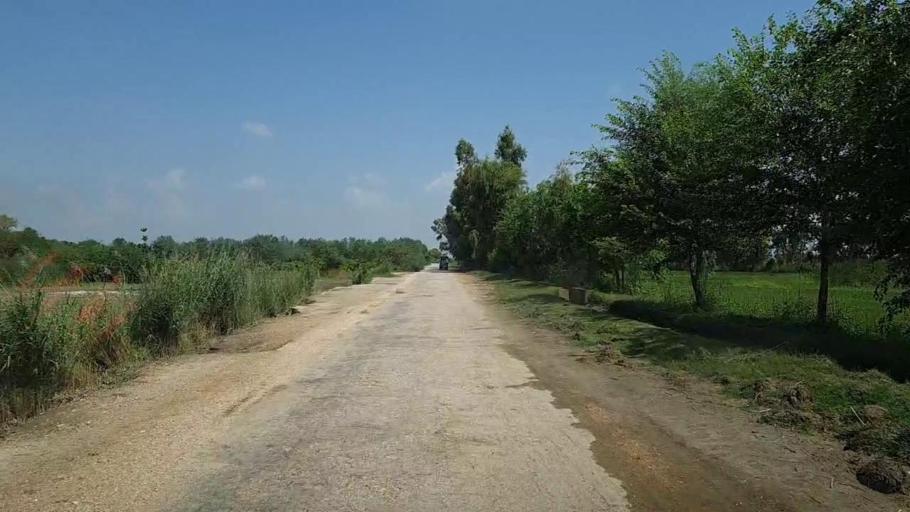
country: PK
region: Sindh
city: Bhiria
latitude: 26.8709
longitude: 68.2549
